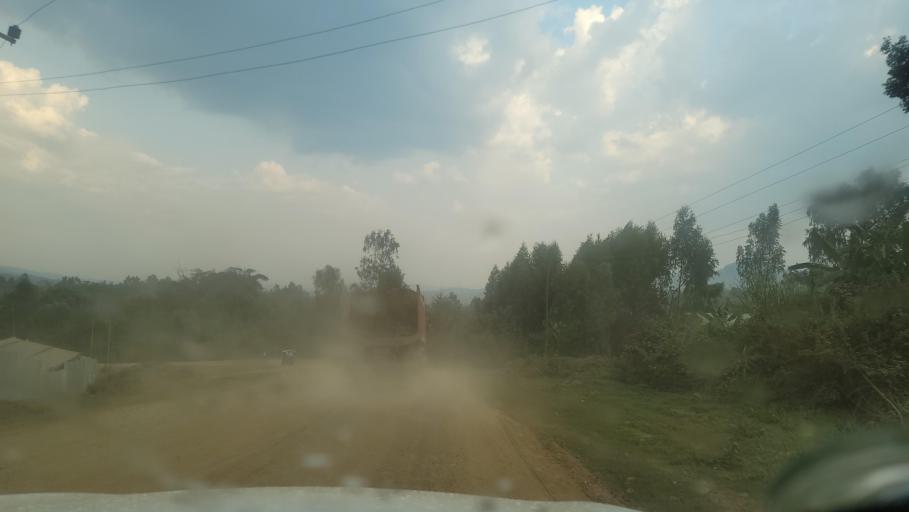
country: ET
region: Oromiya
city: Agaro
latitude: 7.7616
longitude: 36.2888
